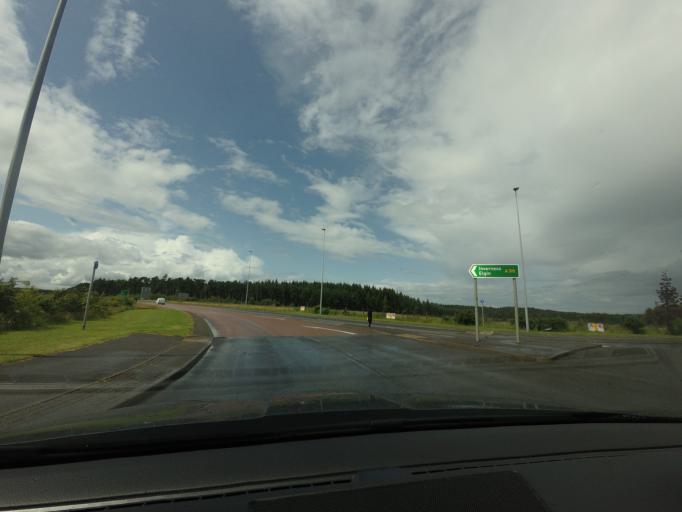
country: GB
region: Scotland
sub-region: Moray
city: Fochabers
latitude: 57.6264
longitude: -3.1425
